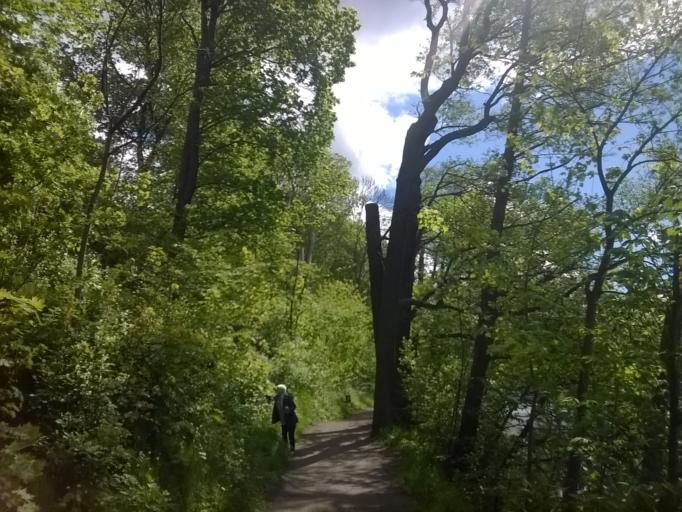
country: SE
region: OEstergoetland
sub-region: Norrkopings Kommun
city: Norrkoping
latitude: 58.5882
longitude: 16.1595
